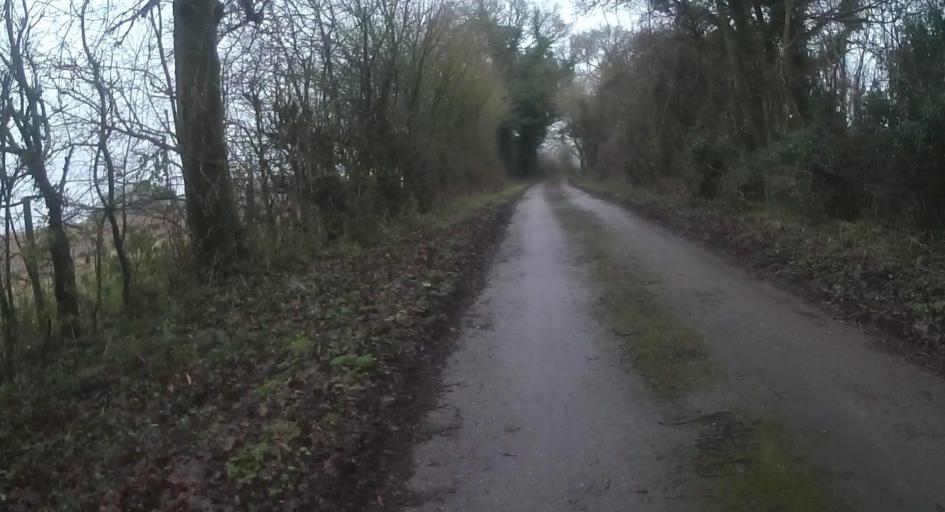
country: GB
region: England
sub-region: Hampshire
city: Kings Worthy
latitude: 51.1064
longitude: -1.2522
